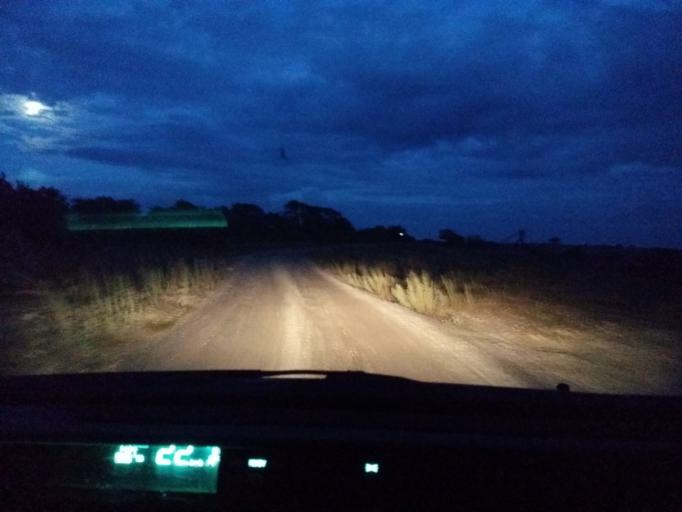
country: SE
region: Kalmar
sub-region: Borgholms Kommun
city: Borgholm
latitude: 57.1157
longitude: 16.8972
